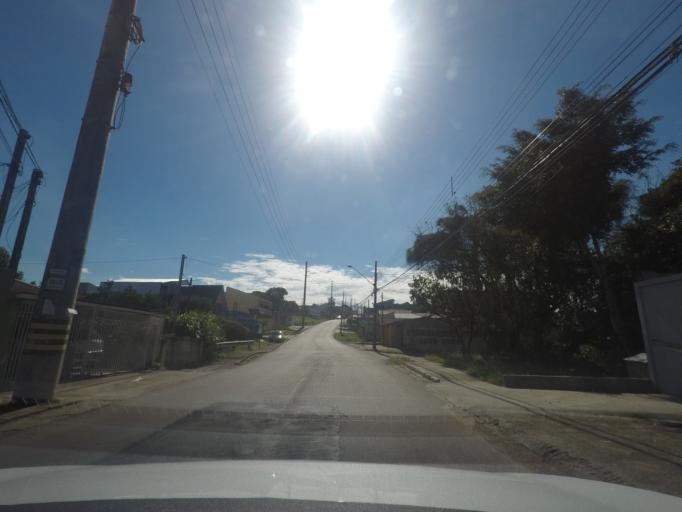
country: BR
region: Parana
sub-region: Sao Jose Dos Pinhais
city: Sao Jose dos Pinhais
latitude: -25.5058
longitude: -49.2783
